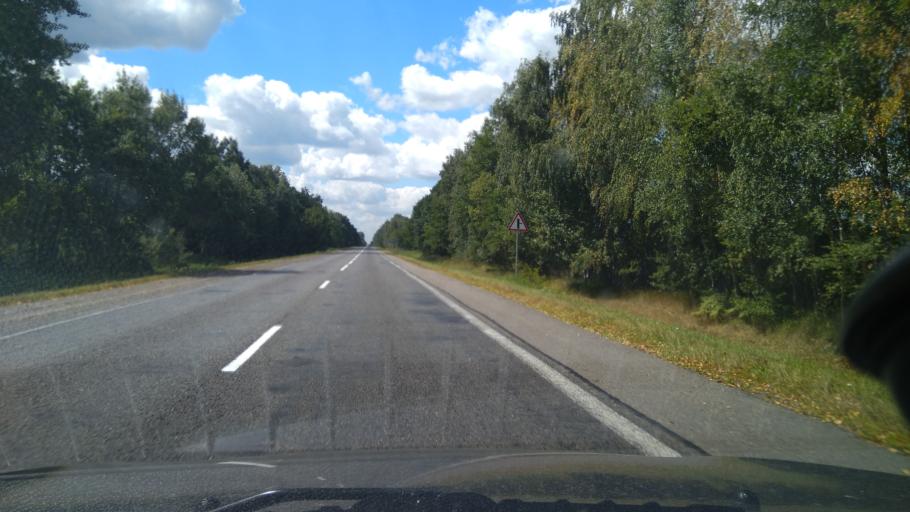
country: BY
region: Brest
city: Ivatsevichy
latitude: 52.6834
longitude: 25.2853
